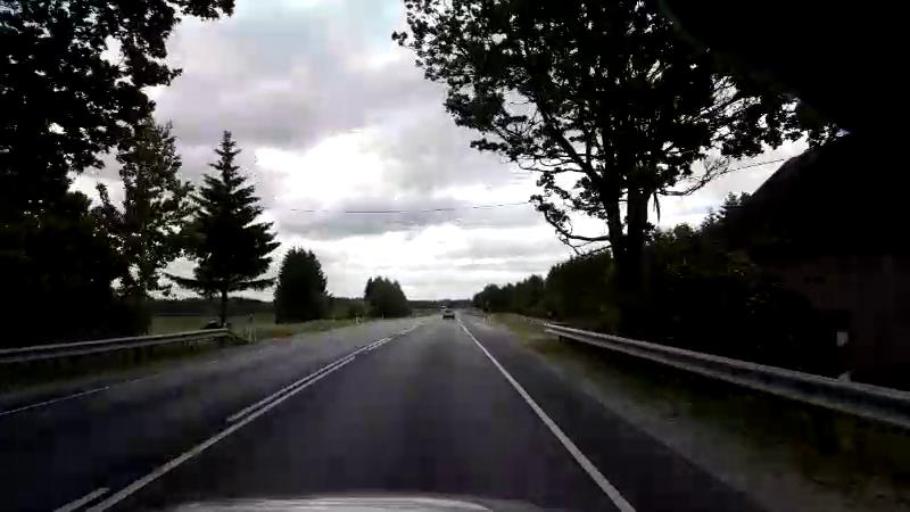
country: EE
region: Paernumaa
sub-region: Halinga vald
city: Parnu-Jaagupi
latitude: 58.6668
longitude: 24.4573
